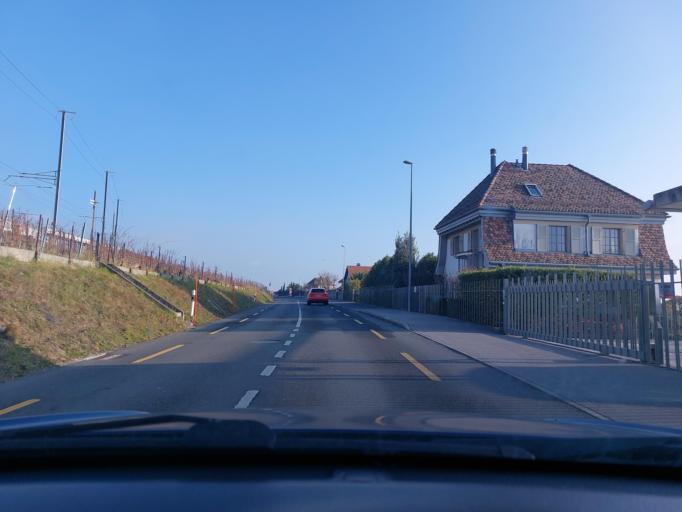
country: CH
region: Vaud
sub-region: Lavaux-Oron District
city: Cully
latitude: 46.4881
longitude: 6.7197
